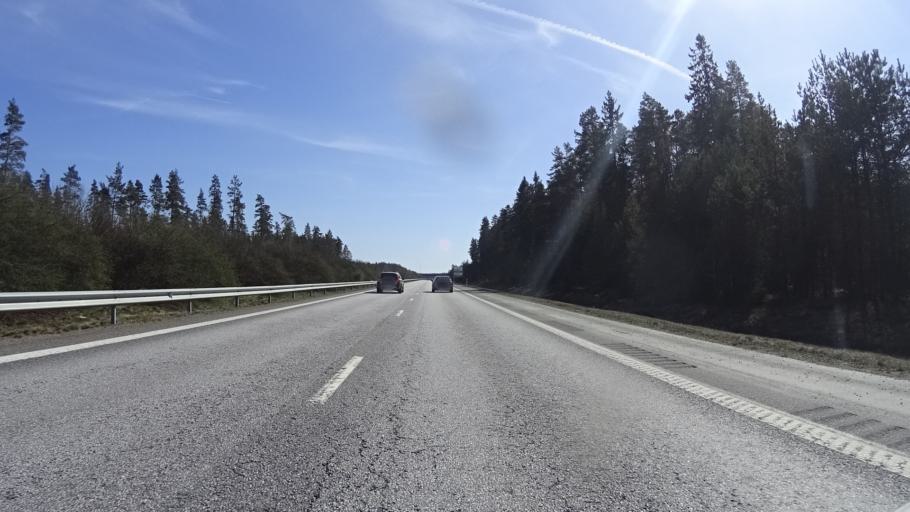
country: SE
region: Joenkoeping
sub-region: Varnamo Kommun
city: Varnamo
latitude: 57.2733
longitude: 14.0822
